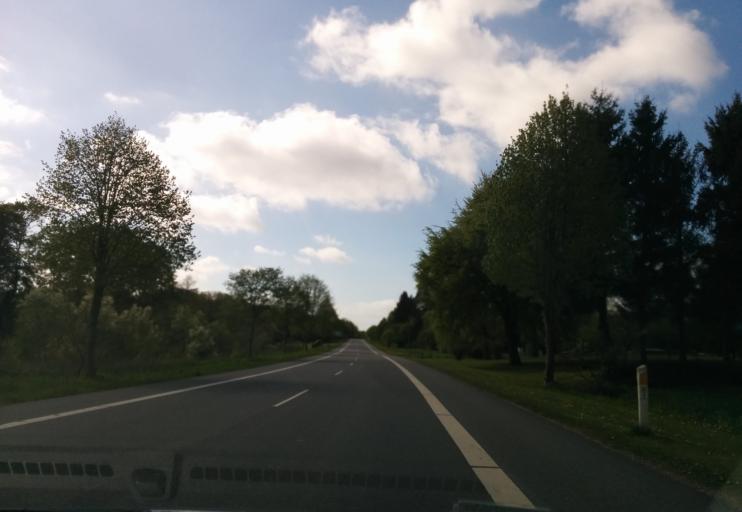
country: DK
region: South Denmark
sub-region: Assens Kommune
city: Arup
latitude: 55.4064
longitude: 10.0795
